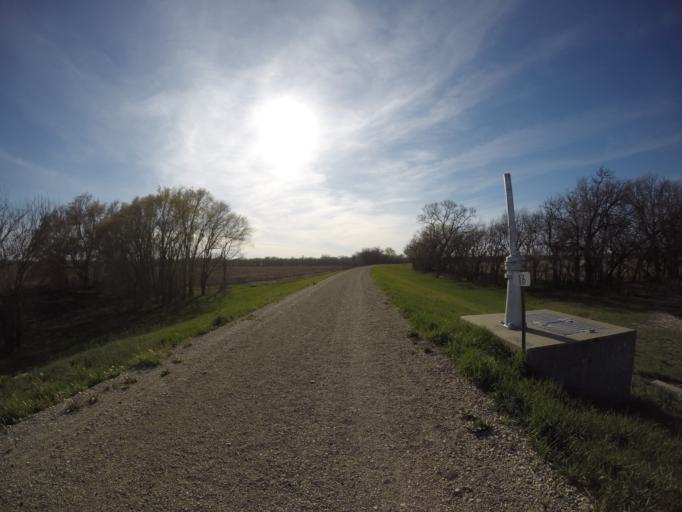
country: US
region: Kansas
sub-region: Saline County
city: Salina
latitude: 38.8633
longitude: -97.5981
